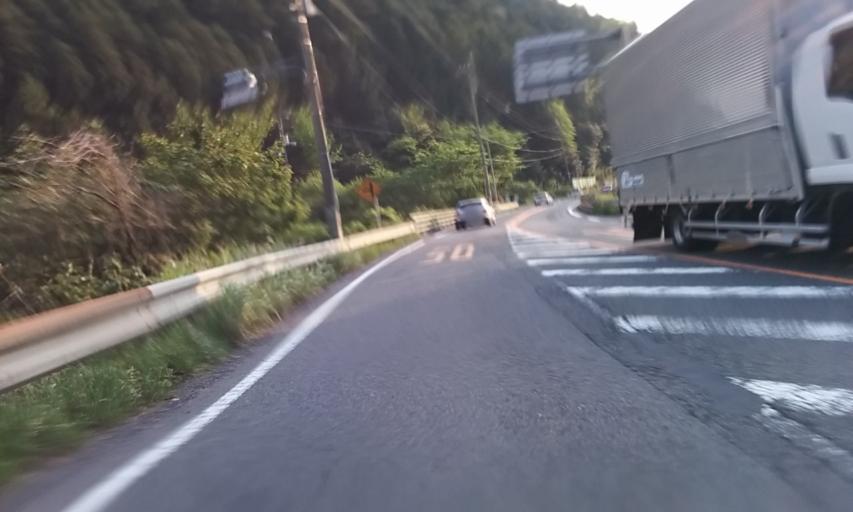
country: JP
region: Ehime
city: Saijo
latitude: 33.8446
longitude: 133.0005
